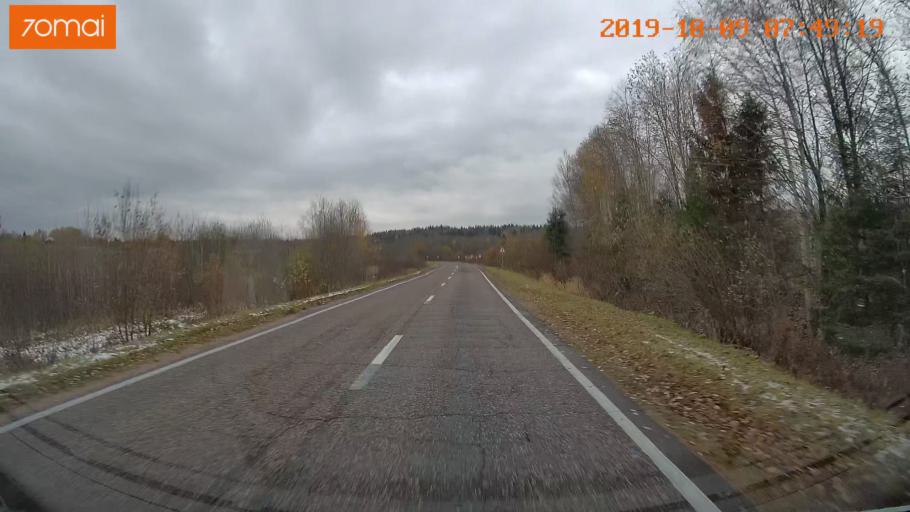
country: RU
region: Jaroslavl
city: Kukoboy
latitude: 58.6675
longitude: 39.8447
